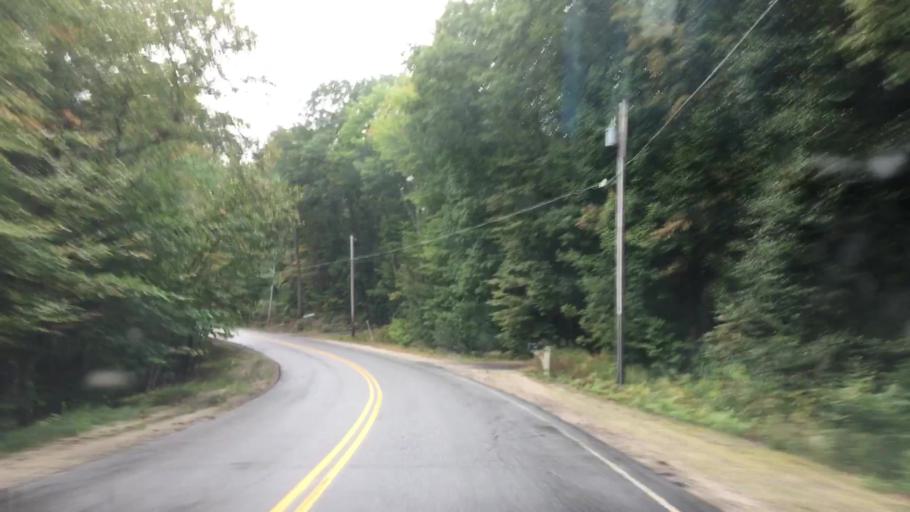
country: US
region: Maine
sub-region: Cumberland County
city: Raymond
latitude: 43.9390
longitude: -70.4303
